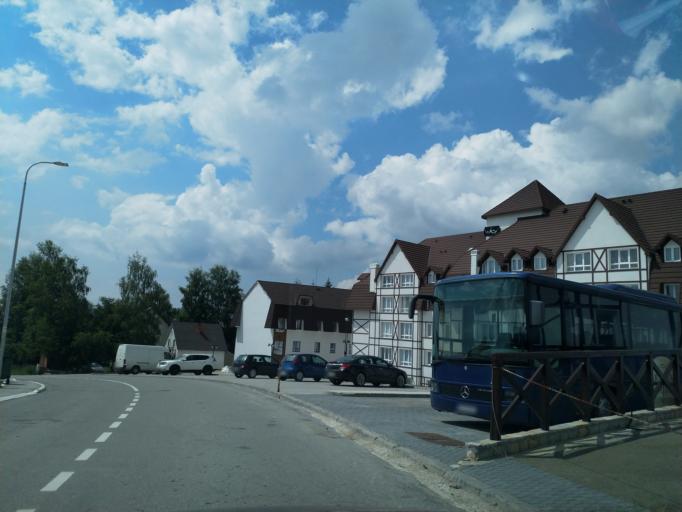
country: RS
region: Central Serbia
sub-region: Raski Okrug
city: Raska
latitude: 43.2749
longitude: 20.7665
